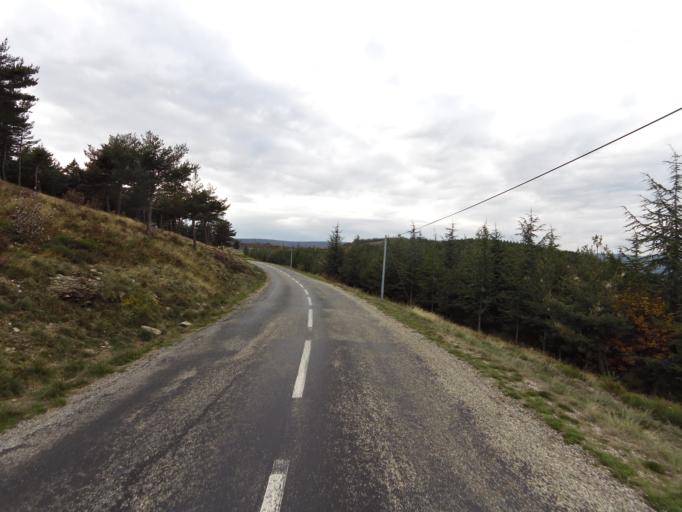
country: FR
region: Rhone-Alpes
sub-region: Departement de l'Ardeche
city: Les Vans
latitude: 44.5018
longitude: 4.0767
